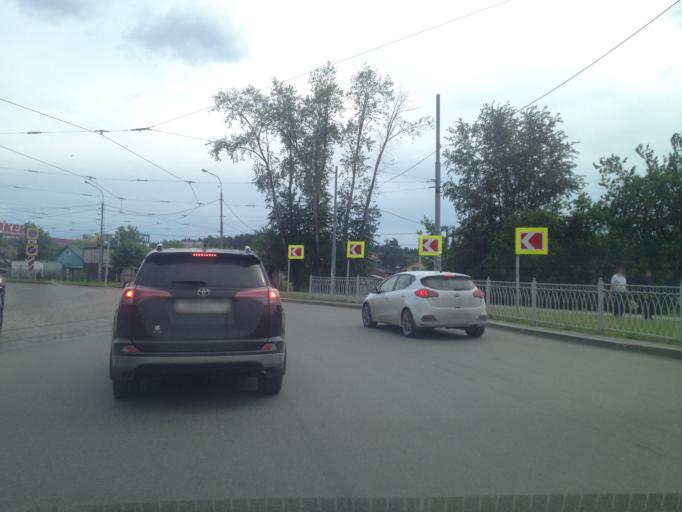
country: RU
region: Sverdlovsk
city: Shirokaya Rechka
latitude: 56.8205
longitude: 60.5364
